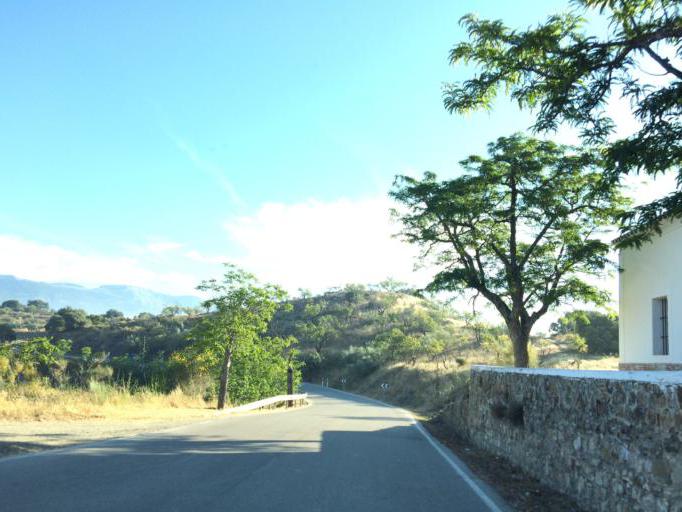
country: ES
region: Andalusia
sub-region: Provincia de Malaga
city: Colmenar
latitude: 36.8943
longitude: -4.3421
